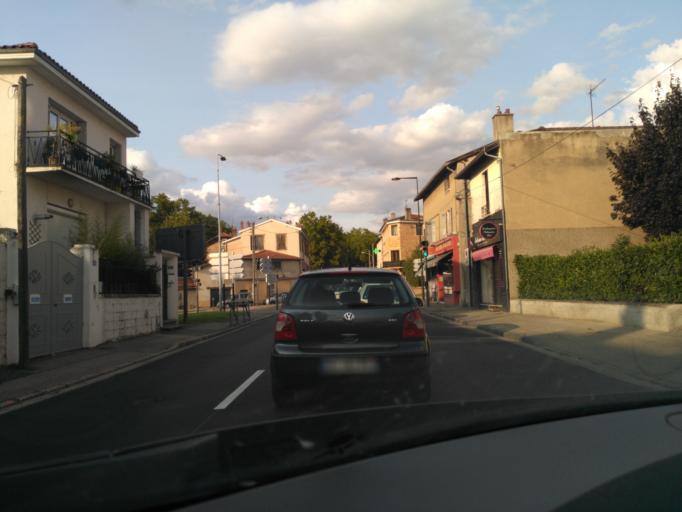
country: FR
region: Rhone-Alpes
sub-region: Departement du Rhone
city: Caluire-et-Cuire
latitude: 45.7912
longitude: 4.8372
